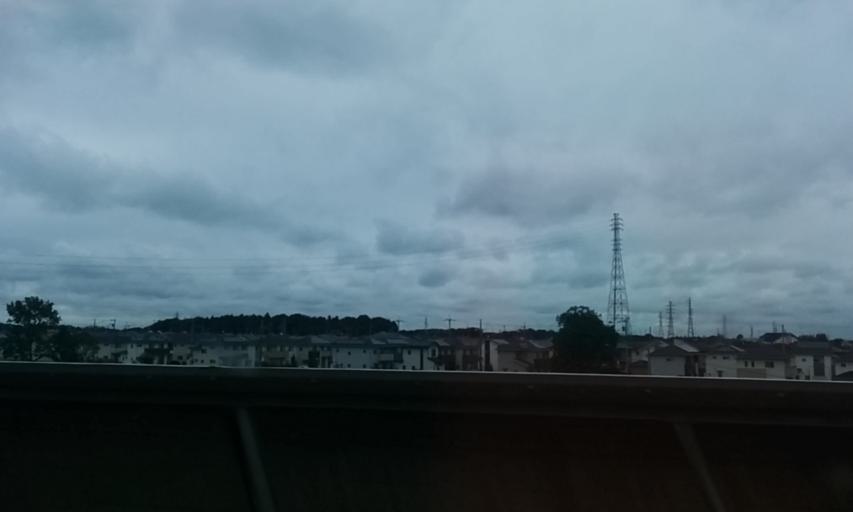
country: JP
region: Ibaraki
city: Koga
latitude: 36.1865
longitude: 139.7419
